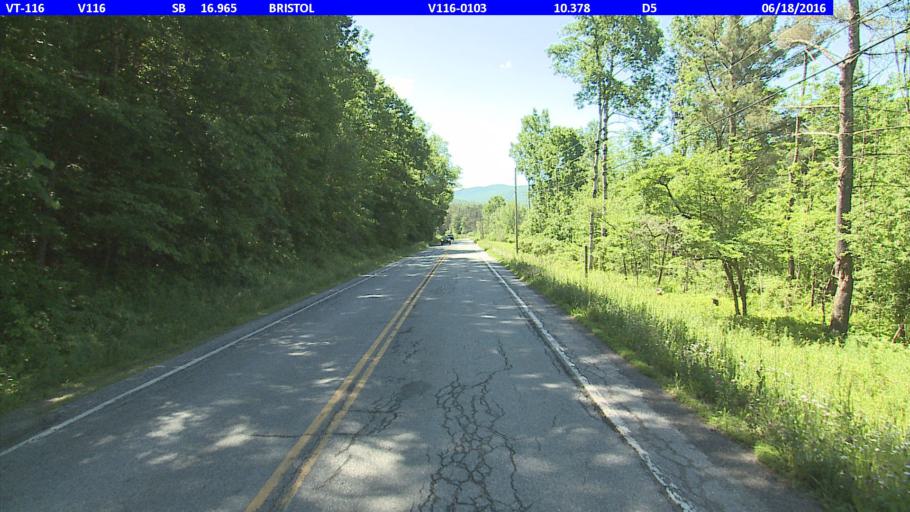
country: US
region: Vermont
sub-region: Addison County
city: Bristol
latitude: 44.1598
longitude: -73.0496
